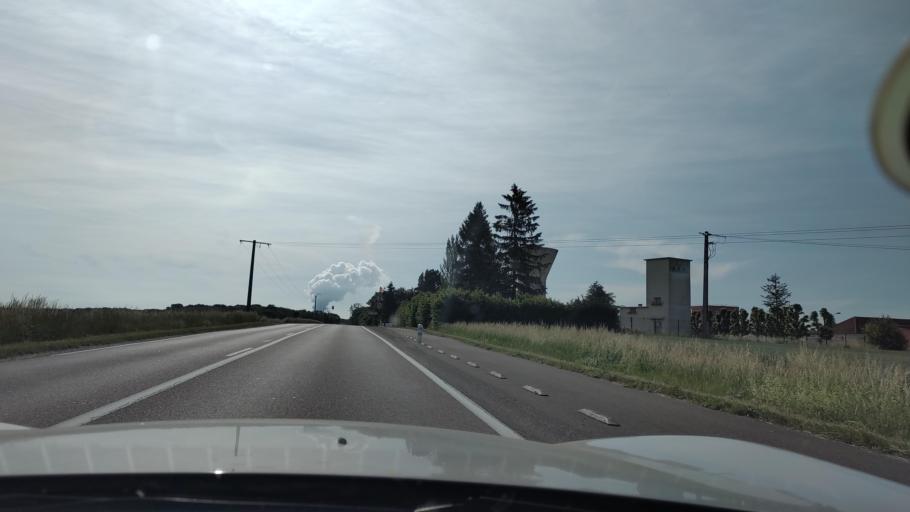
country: FR
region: Ile-de-France
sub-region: Departement de Seine-et-Marne
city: Sourdun
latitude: 48.5342
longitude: 3.3689
